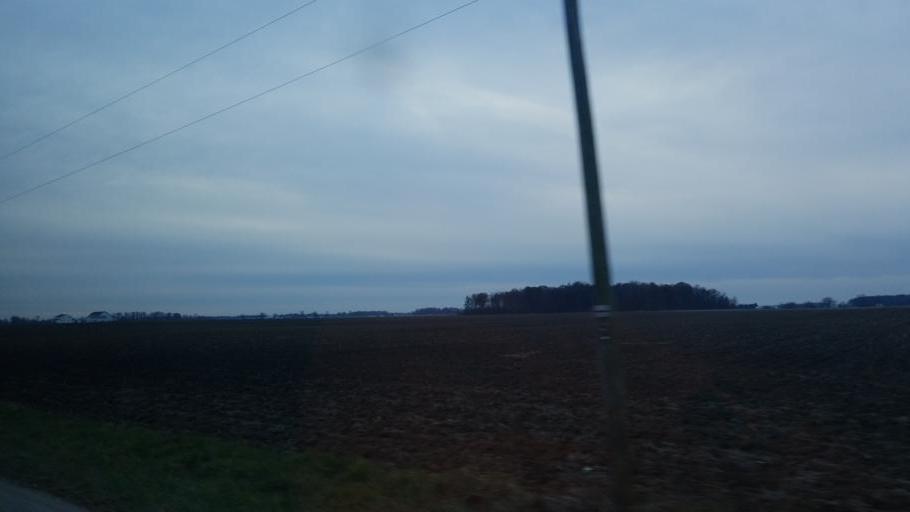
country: US
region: Indiana
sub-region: Adams County
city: Decatur
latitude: 40.7885
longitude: -84.8801
